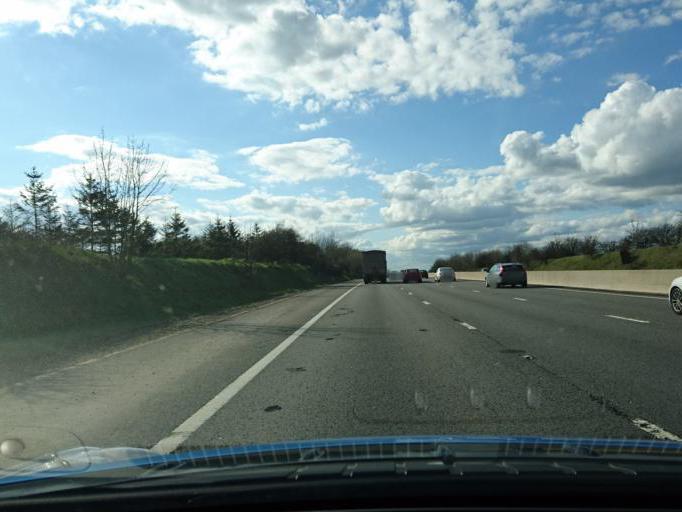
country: GB
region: England
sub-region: Wiltshire
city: Aldbourne
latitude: 51.5088
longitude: -1.6132
